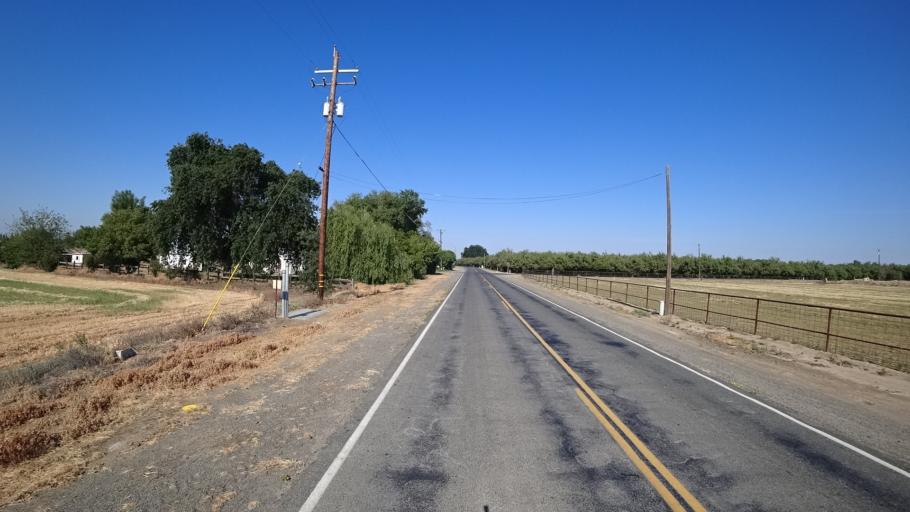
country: US
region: California
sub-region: Kings County
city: Lemoore
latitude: 36.3658
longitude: -119.8152
